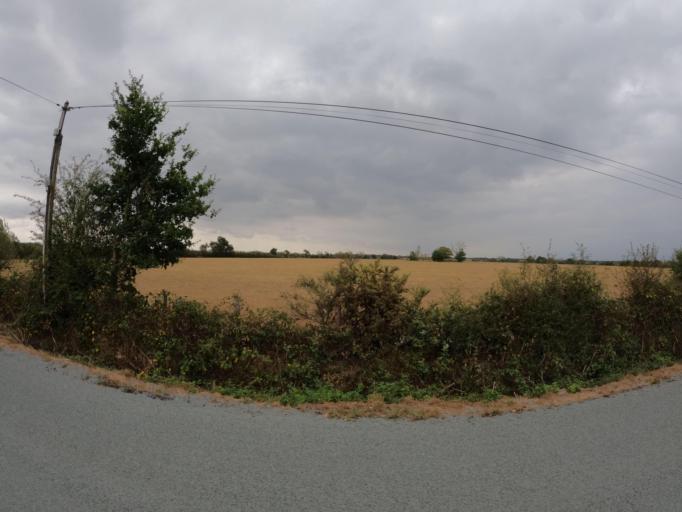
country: FR
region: Pays de la Loire
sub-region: Departement de la Vendee
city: Treize-Septiers
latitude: 46.9782
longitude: -1.2063
